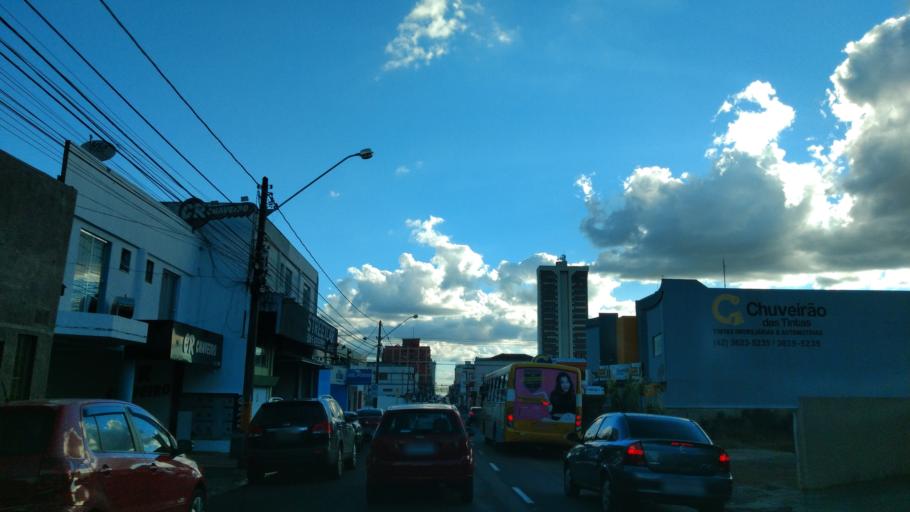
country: BR
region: Parana
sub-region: Guarapuava
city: Guarapuava
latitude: -25.3899
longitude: -51.4655
